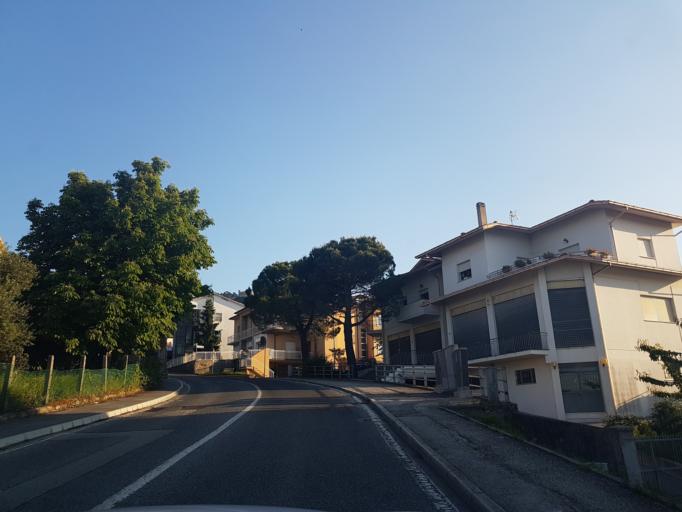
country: SM
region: Borgo Maggiore
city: Borgo Maggiore
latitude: 43.9491
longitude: 12.4521
